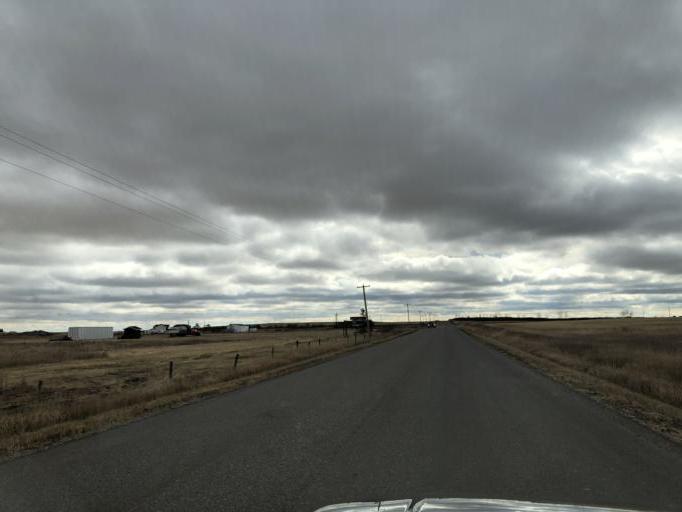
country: CA
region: Alberta
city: Chestermere
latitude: 50.9202
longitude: -113.8830
